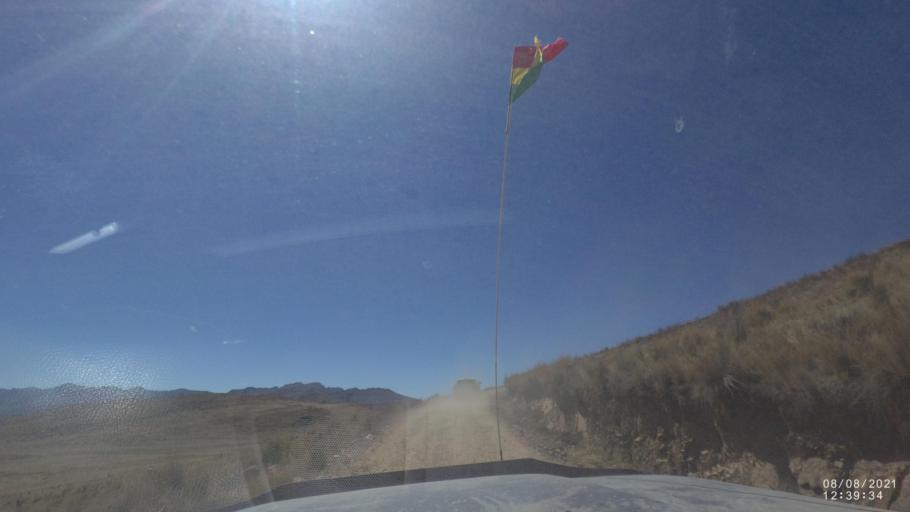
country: BO
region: Cochabamba
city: Colchani
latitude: -16.8277
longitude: -66.6242
